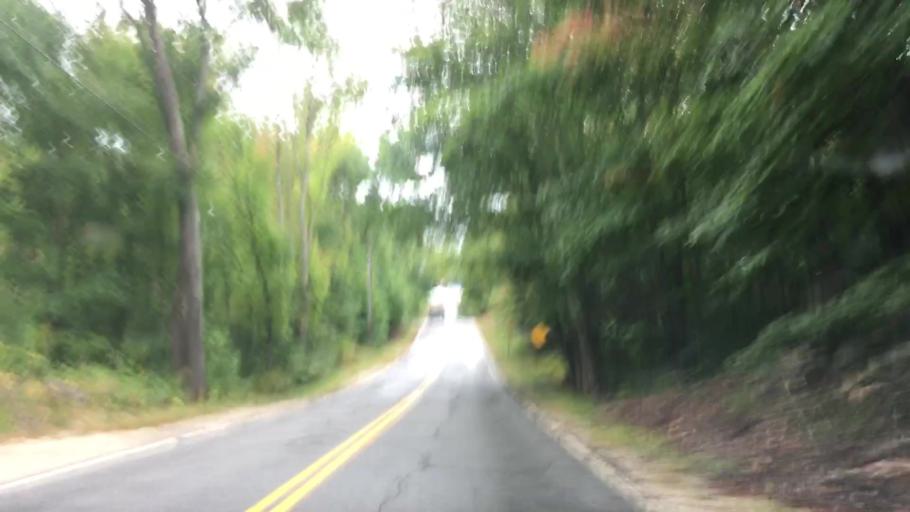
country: US
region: Maine
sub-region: Cumberland County
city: Raymond
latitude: 43.9758
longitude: -70.4701
